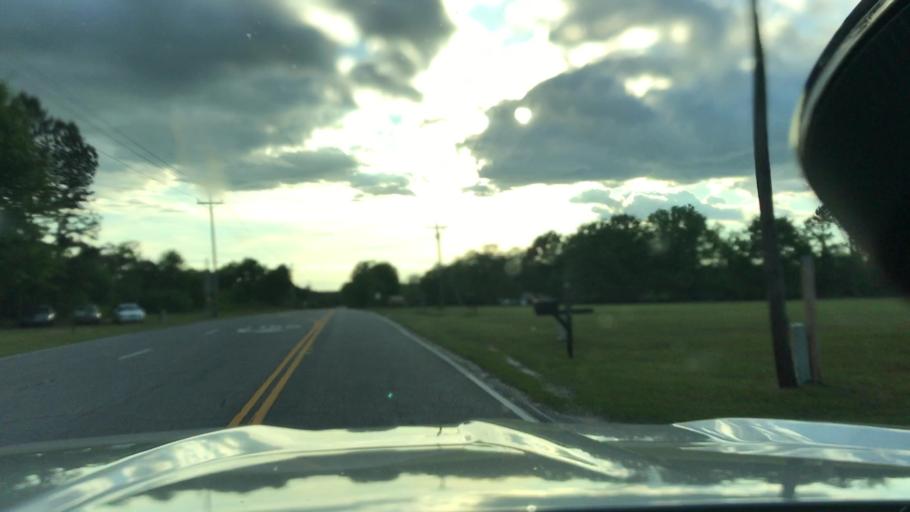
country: US
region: South Carolina
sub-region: Barnwell County
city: Blackville
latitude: 33.4739
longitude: -81.1898
